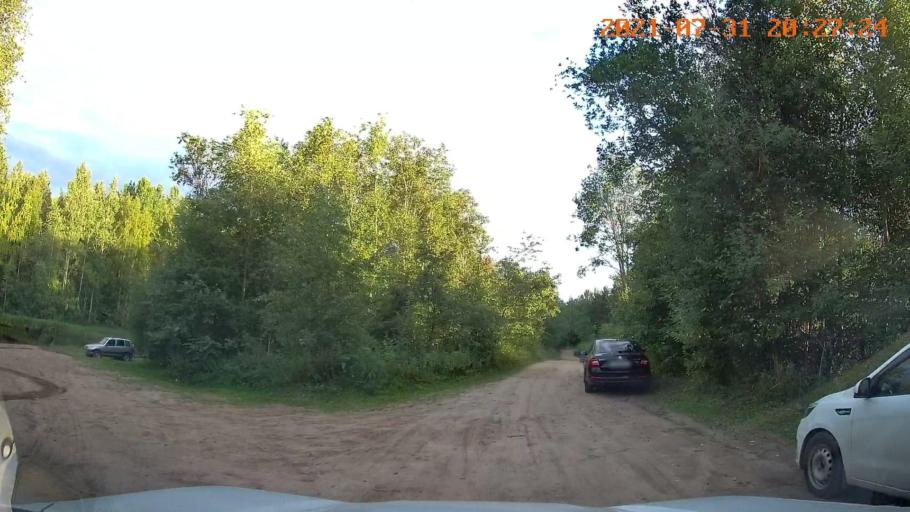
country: RU
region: Republic of Karelia
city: Pudozh
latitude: 61.6666
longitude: 36.3042
